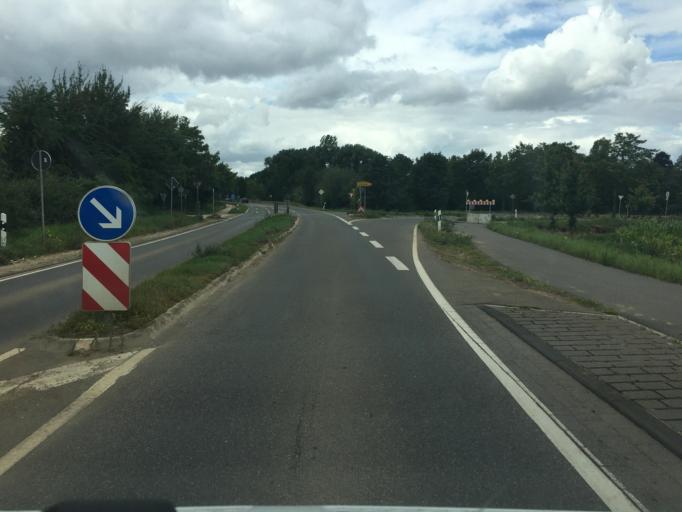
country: DE
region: North Rhine-Westphalia
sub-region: Regierungsbezirk Koln
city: Euskirchen
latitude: 50.6484
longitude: 6.7516
